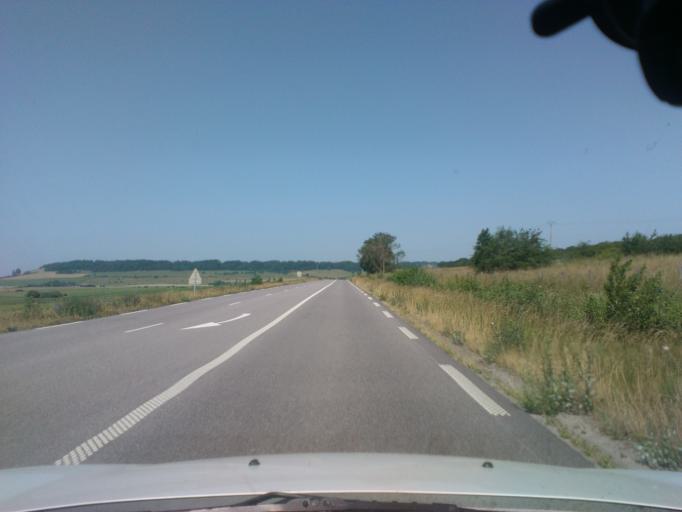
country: FR
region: Lorraine
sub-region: Departement des Vosges
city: Chatenois
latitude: 48.3011
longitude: 5.8126
